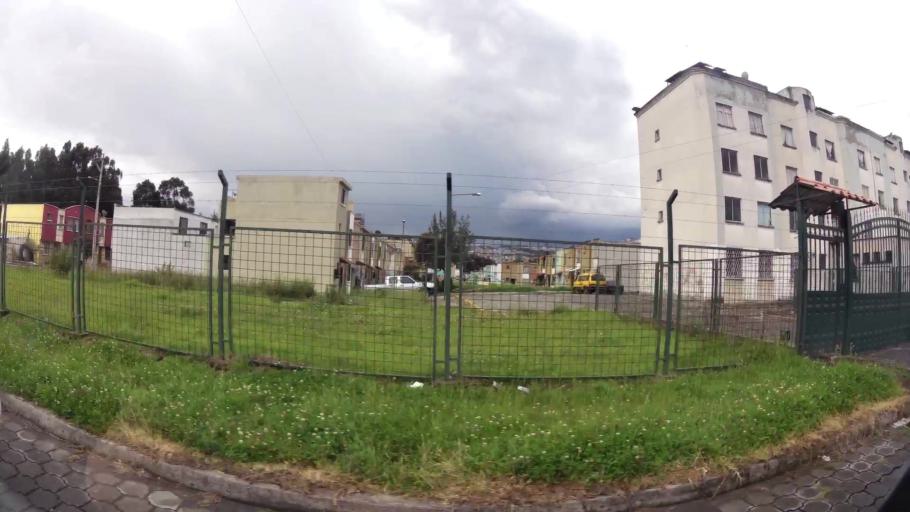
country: EC
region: Pichincha
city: Quito
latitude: -0.2891
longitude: -78.5534
